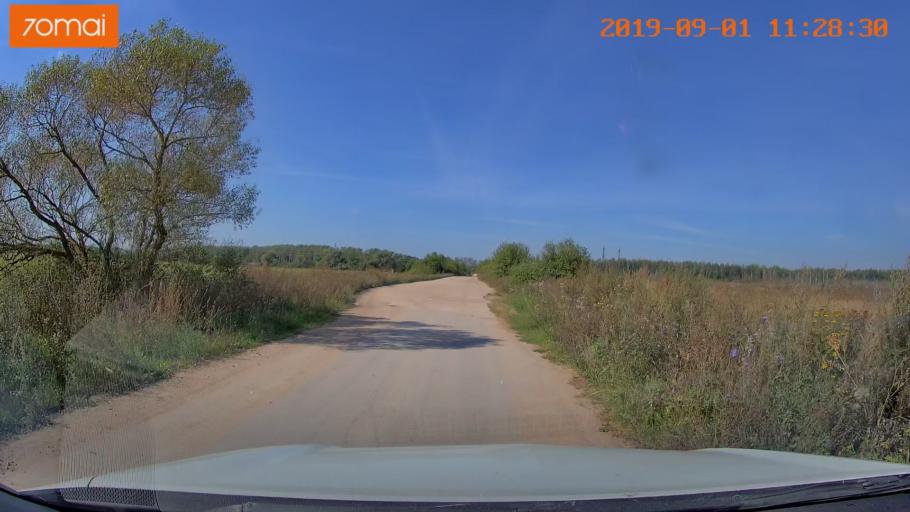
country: RU
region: Kaluga
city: Detchino
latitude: 54.8332
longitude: 36.3487
